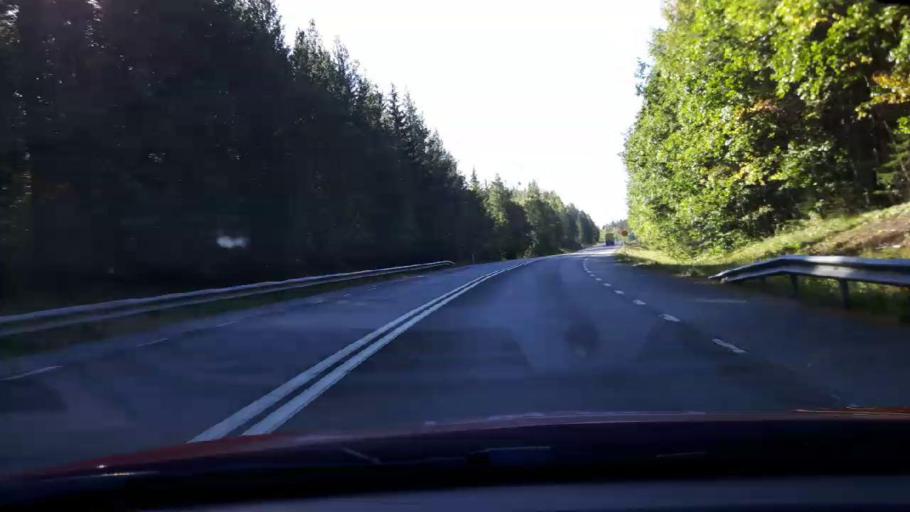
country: SE
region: Jaemtland
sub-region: Braecke Kommun
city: Braecke
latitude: 62.7364
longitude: 15.4331
